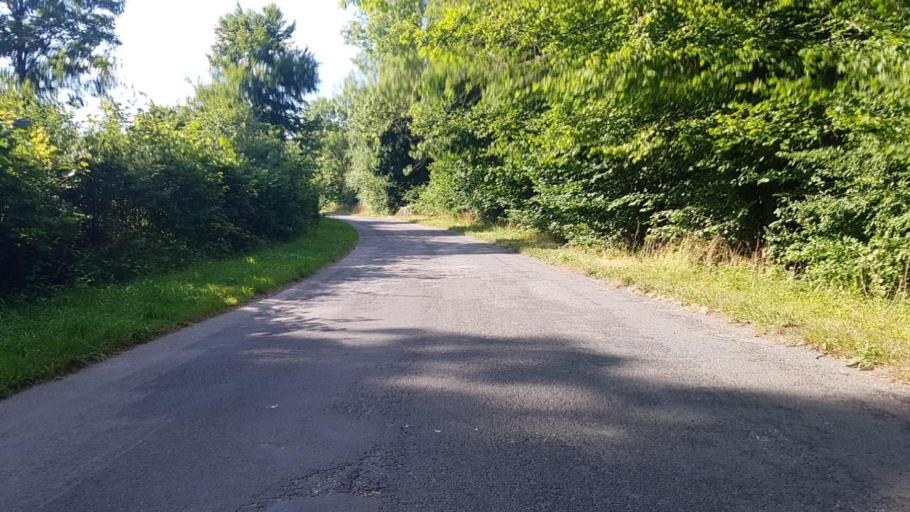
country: FR
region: Picardie
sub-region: Departement de l'Oise
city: Senlis
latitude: 49.1943
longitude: 2.6065
